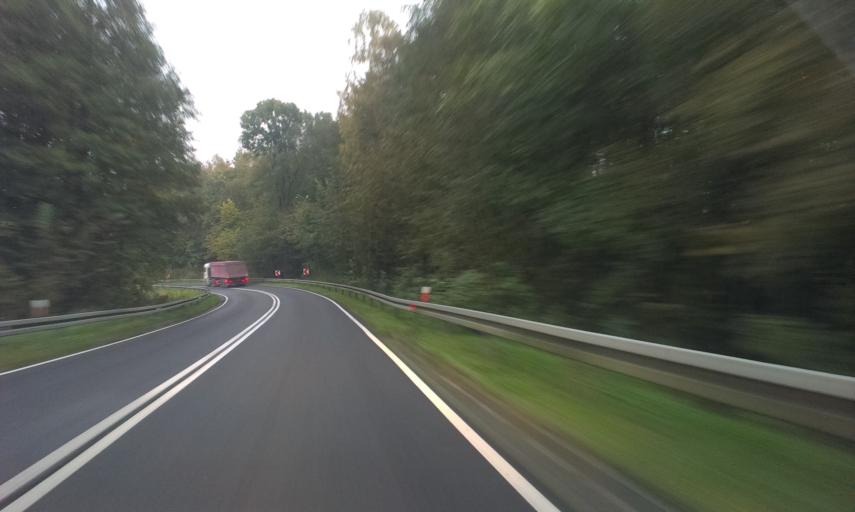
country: PL
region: Kujawsko-Pomorskie
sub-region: Powiat sepolenski
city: Sosno
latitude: 53.4381
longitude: 17.6371
